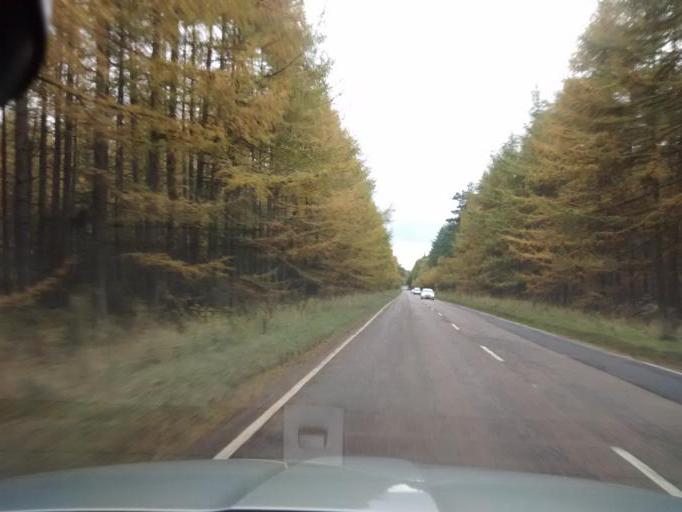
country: GB
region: Scotland
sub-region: Perth and Kinross
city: Blairgowrie
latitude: 56.5469
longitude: -3.3542
